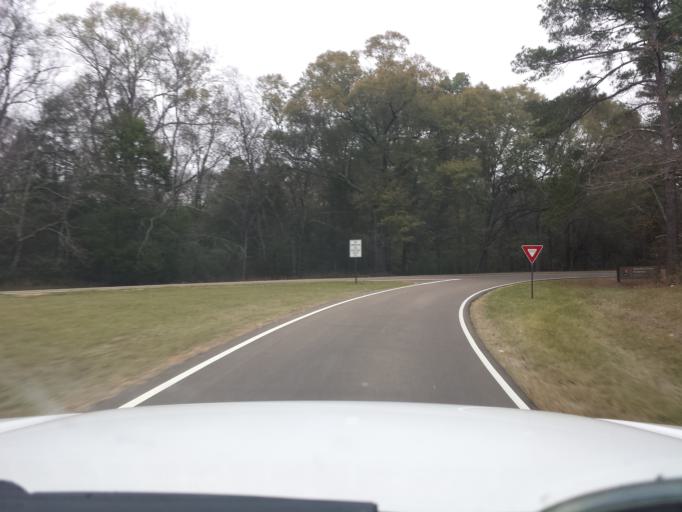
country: US
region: Mississippi
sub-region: Madison County
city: Canton
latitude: 32.5264
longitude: -89.9764
